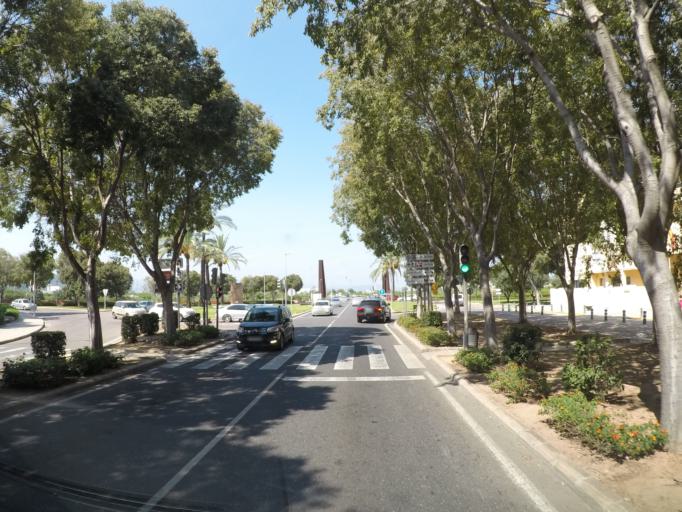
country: ES
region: Valencia
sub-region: Provincia de Valencia
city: Oliva
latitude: 38.9239
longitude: -0.1254
